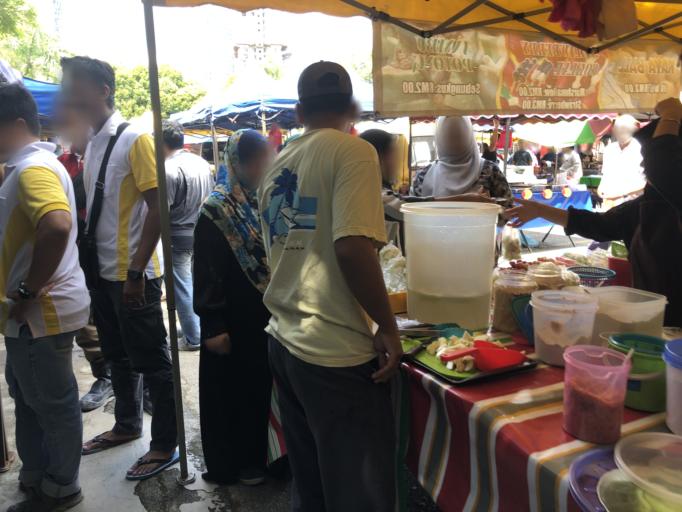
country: MY
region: Kuala Lumpur
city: Kuala Lumpur
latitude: 3.1735
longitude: 101.6721
